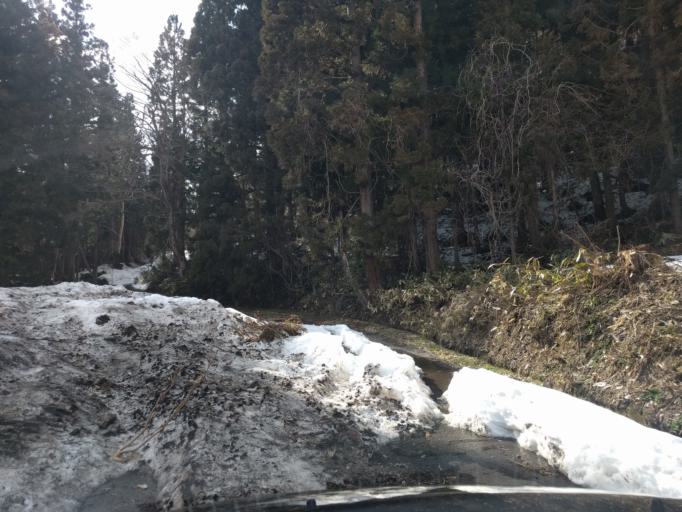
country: JP
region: Fukushima
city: Kitakata
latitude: 37.4507
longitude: 139.7952
